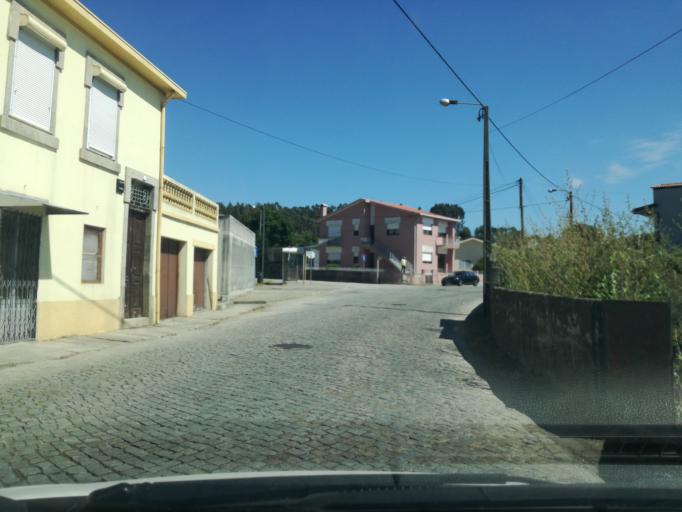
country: PT
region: Porto
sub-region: Maia
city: Anta
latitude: 41.2753
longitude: -8.6339
